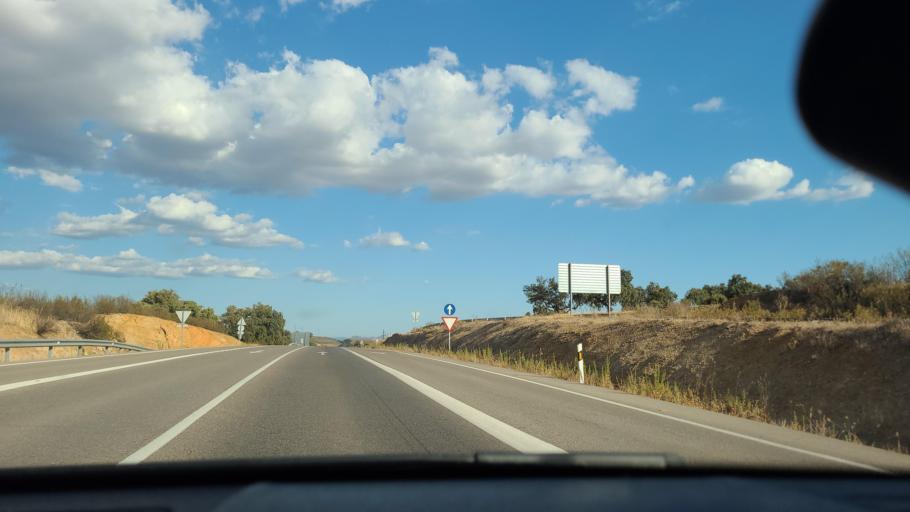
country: ES
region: Andalusia
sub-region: Province of Cordoba
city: Belmez
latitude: 38.2874
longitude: -5.2202
